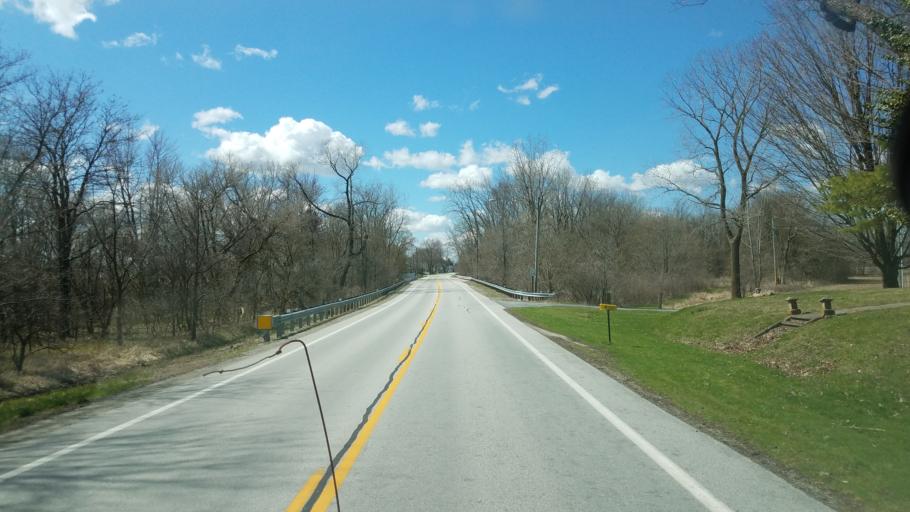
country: US
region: Ohio
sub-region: Sandusky County
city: Ballville
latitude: 41.2508
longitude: -83.2284
